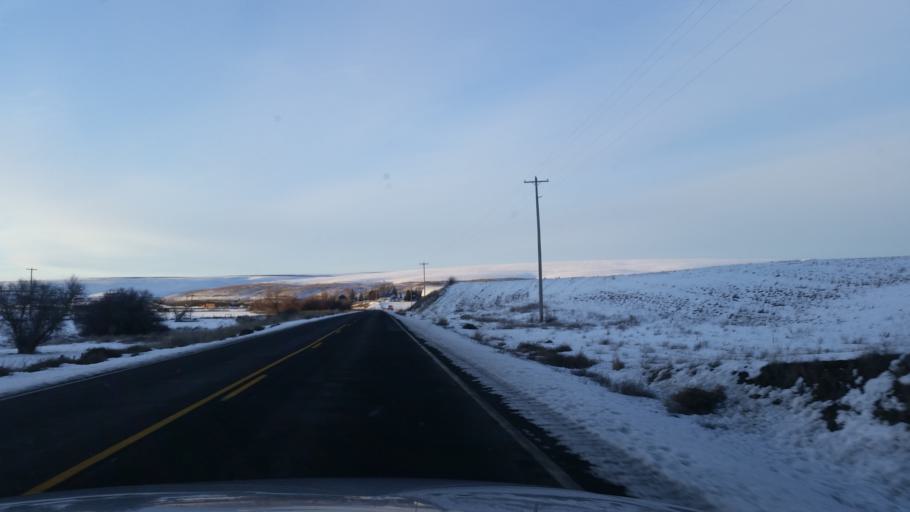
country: US
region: Washington
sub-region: Whitman County
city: Colfax
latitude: 47.1129
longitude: -117.6393
